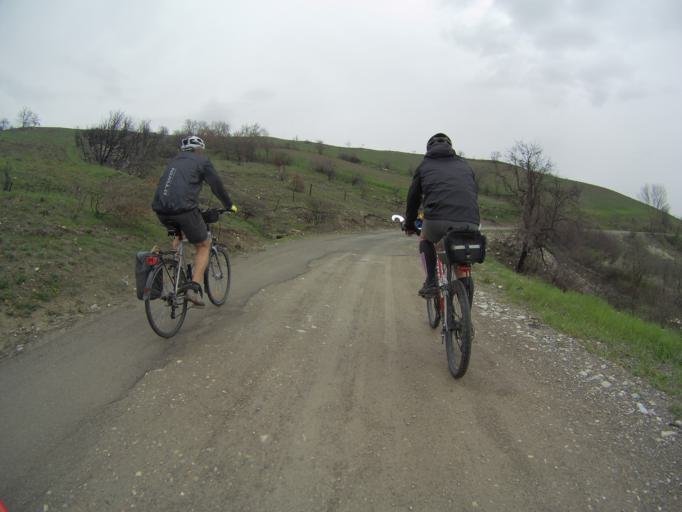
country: IT
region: Emilia-Romagna
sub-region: Provincia di Reggio Emilia
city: Casina
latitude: 44.5384
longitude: 10.4458
